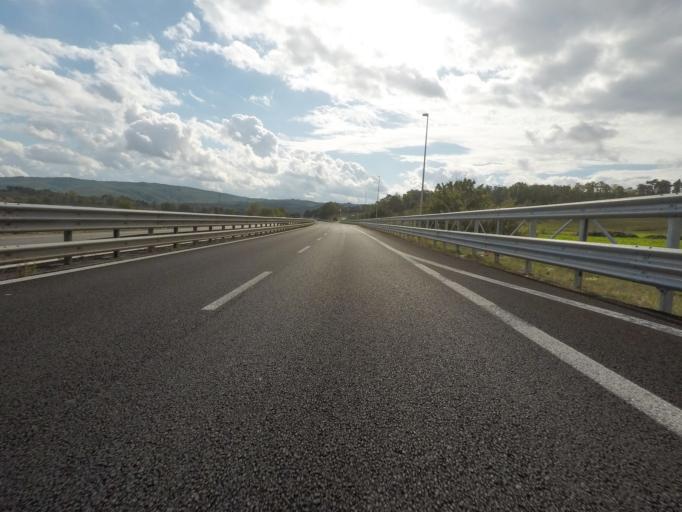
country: IT
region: Tuscany
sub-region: Provincia di Siena
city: Serre di Rapolano
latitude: 43.2571
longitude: 11.6329
